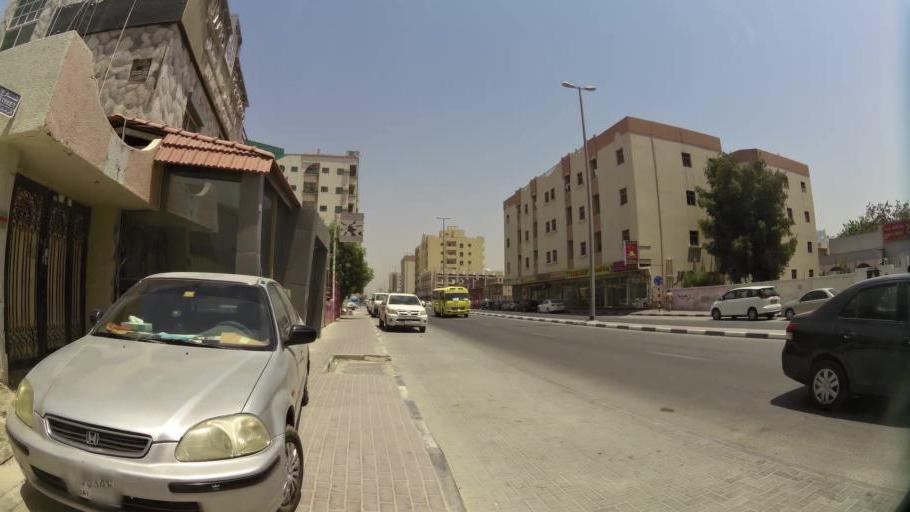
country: AE
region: Ajman
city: Ajman
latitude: 25.4056
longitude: 55.4337
